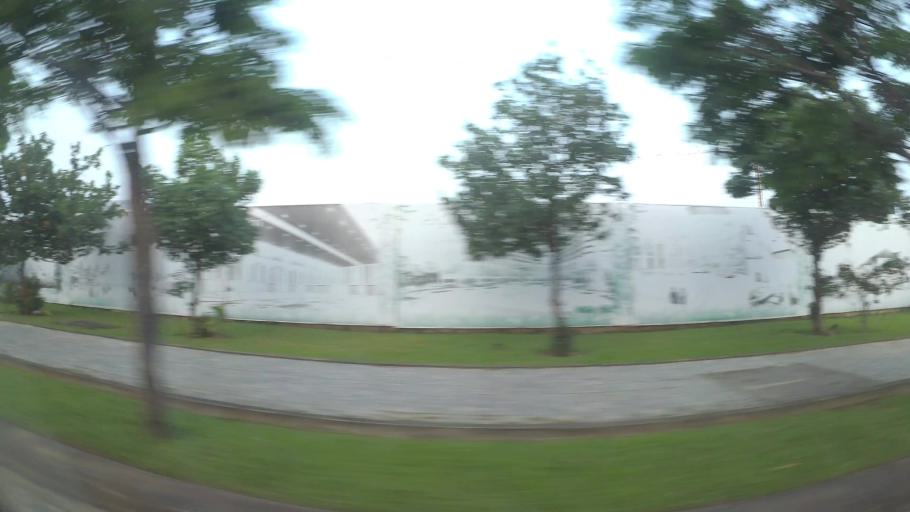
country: VN
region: Da Nang
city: Ngu Hanh Son
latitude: 16.0332
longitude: 108.2527
